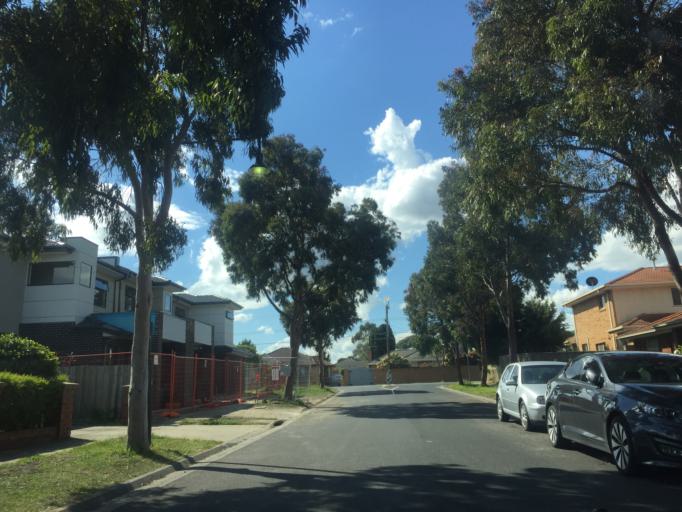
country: AU
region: Victoria
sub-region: Darebin
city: Kingsbury
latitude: -37.7138
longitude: 145.0285
